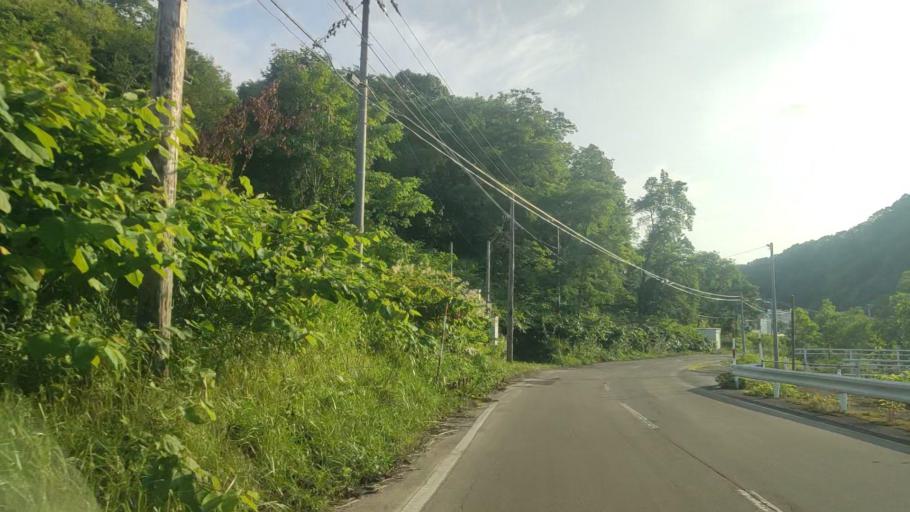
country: JP
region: Hokkaido
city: Iwamizawa
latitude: 43.0624
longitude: 141.9824
